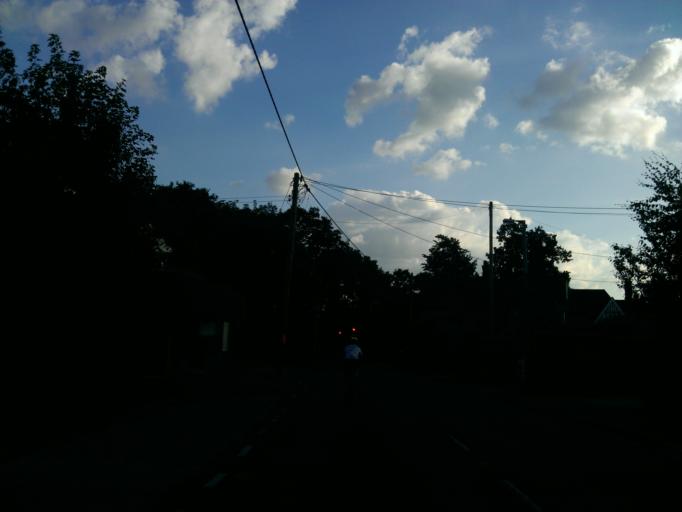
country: GB
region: England
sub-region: Essex
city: Braintree
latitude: 51.9157
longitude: 0.5824
